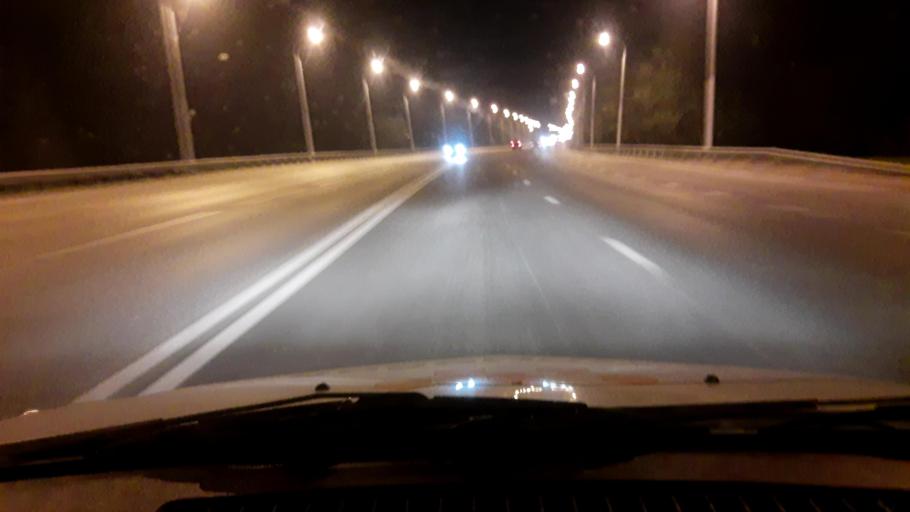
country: RU
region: Bashkortostan
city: Iglino
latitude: 54.7982
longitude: 56.2040
